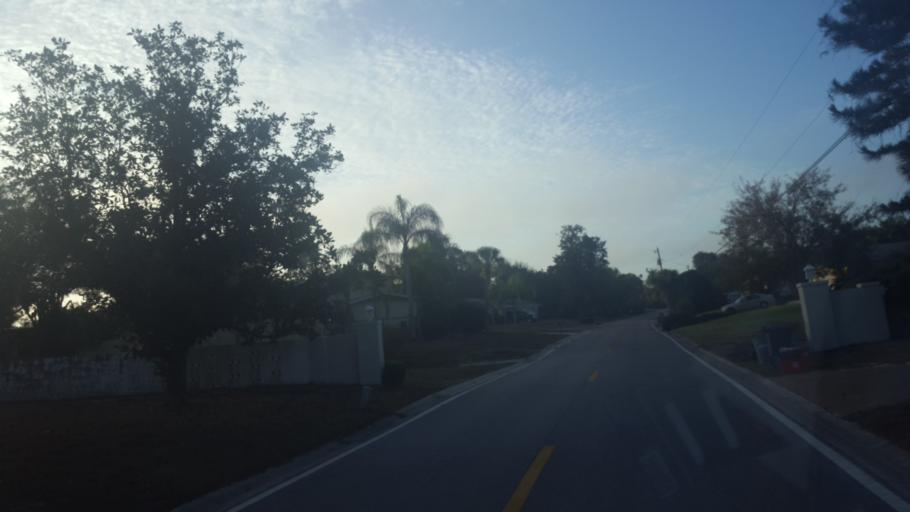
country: US
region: Florida
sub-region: Sarasota County
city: Southgate
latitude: 27.3120
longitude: -82.5081
